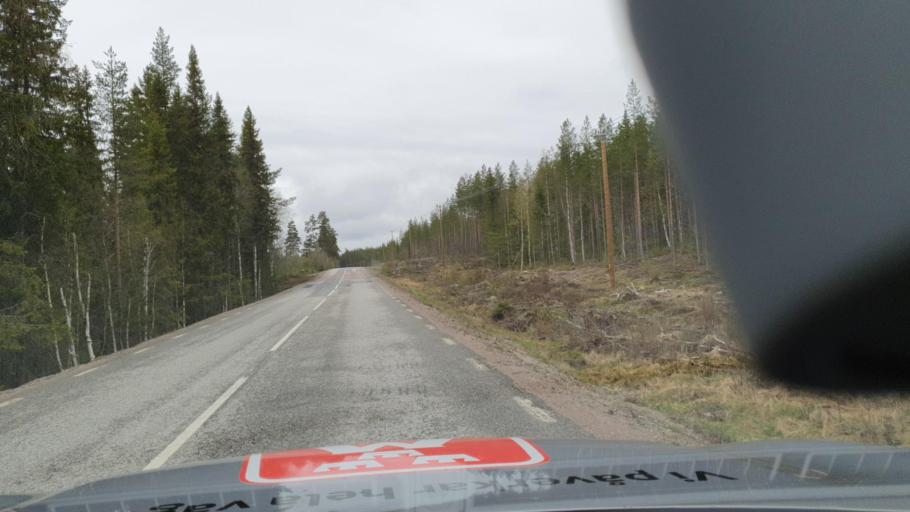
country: SE
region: Vaesternorrland
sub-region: Solleftea Kommun
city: Solleftea
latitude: 63.6265
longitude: 17.4501
